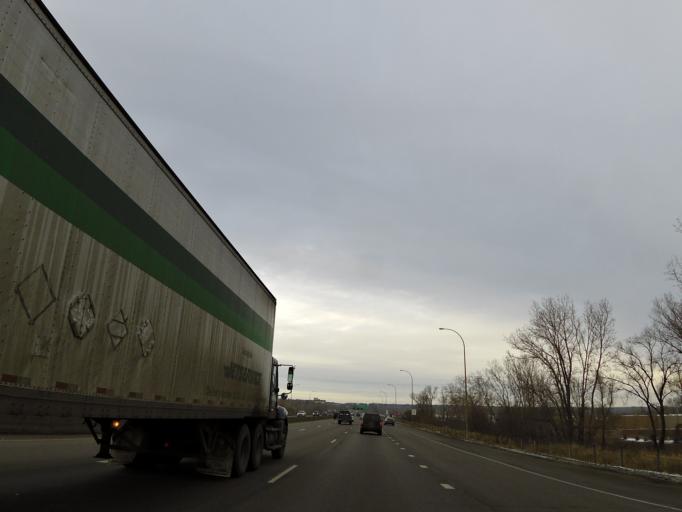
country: US
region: Minnesota
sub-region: Dakota County
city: Burnsville
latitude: 44.7783
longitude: -93.2882
